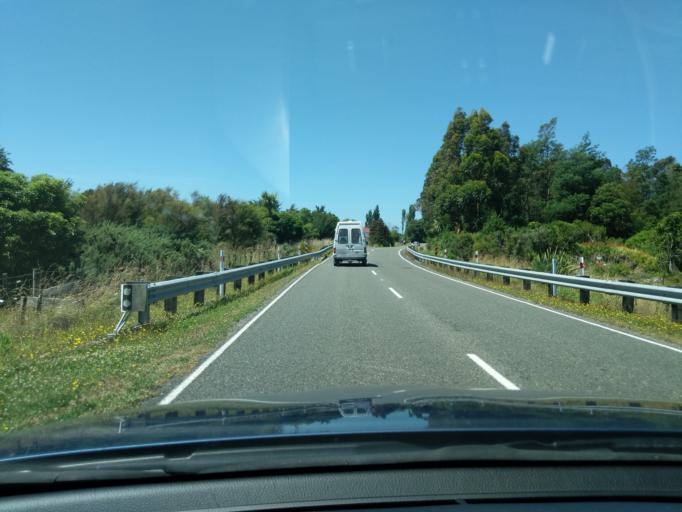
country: NZ
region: Tasman
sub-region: Tasman District
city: Takaka
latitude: -40.6833
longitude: 172.6617
